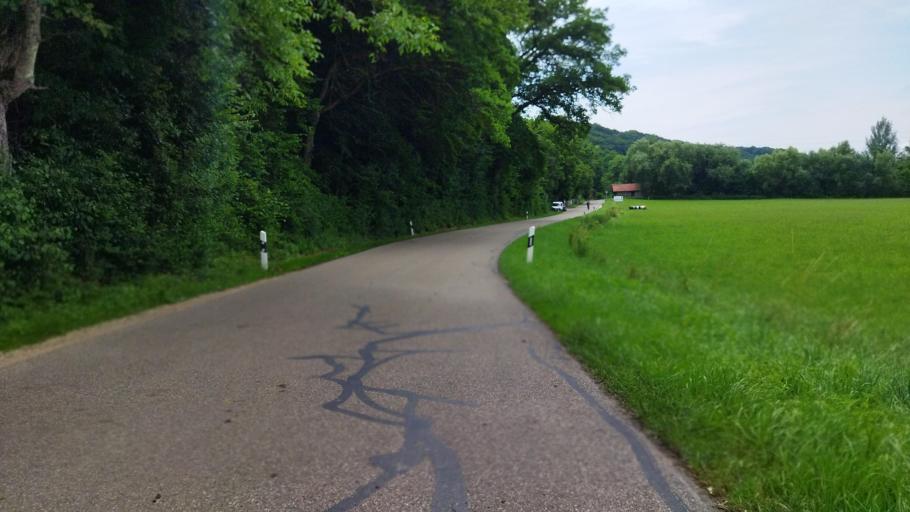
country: DE
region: Bavaria
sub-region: Upper Palatinate
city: Pentling
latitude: 48.9855
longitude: 12.0466
